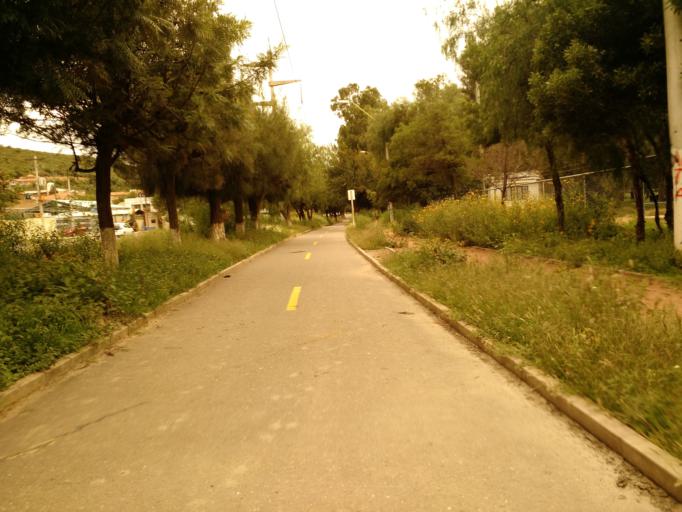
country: BO
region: Cochabamba
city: Cochabamba
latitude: -17.4083
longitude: -66.1274
